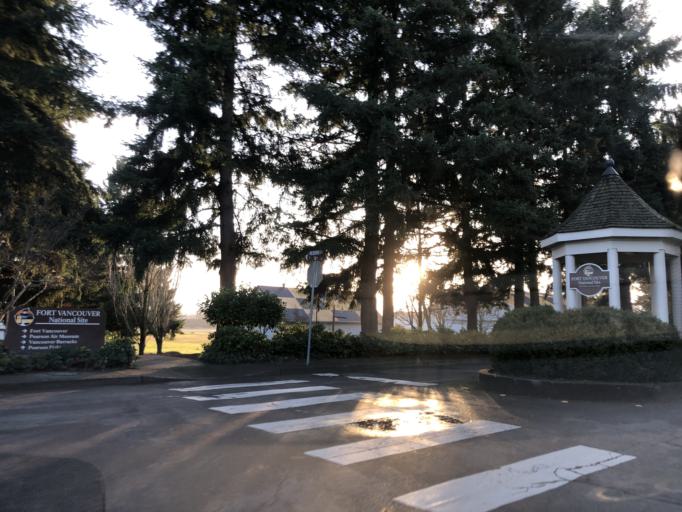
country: US
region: Washington
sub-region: Clark County
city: Vancouver
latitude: 45.6247
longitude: -122.6547
